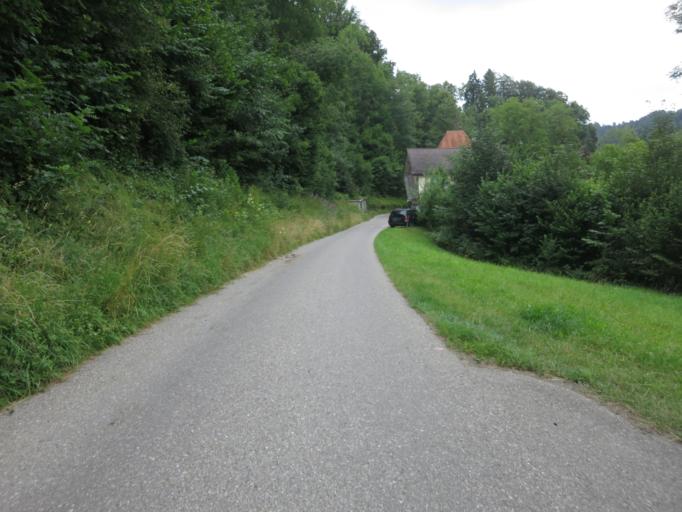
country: CH
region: Saint Gallen
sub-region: Wahlkreis Toggenburg
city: Buetschwil
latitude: 47.3559
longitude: 9.0783
